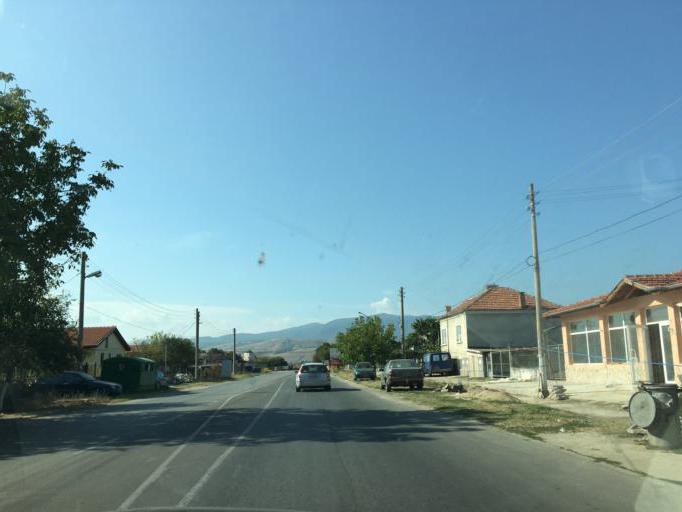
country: BG
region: Pazardzhik
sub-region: Obshtina Pazardzhik
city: Pazardzhik
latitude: 42.1548
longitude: 24.3110
